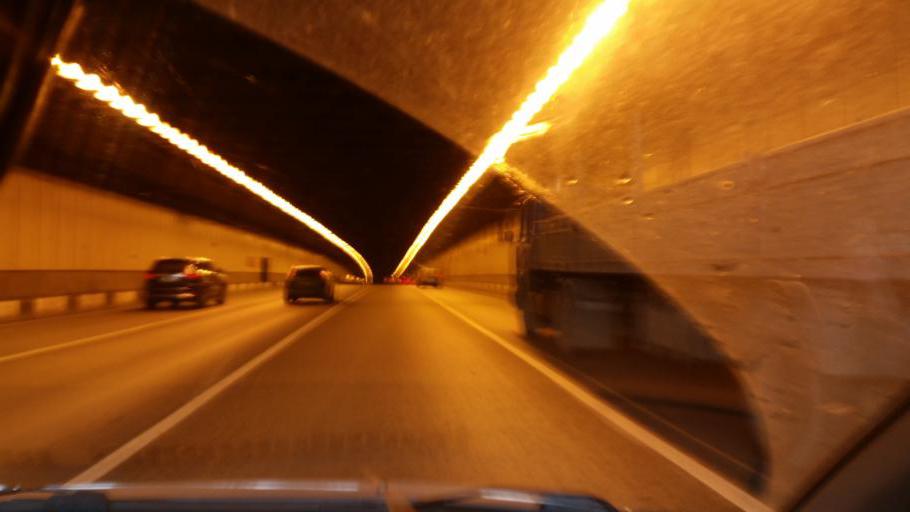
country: RU
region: Moscow
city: Novyye Cheremushki
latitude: 55.7121
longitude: 37.5796
